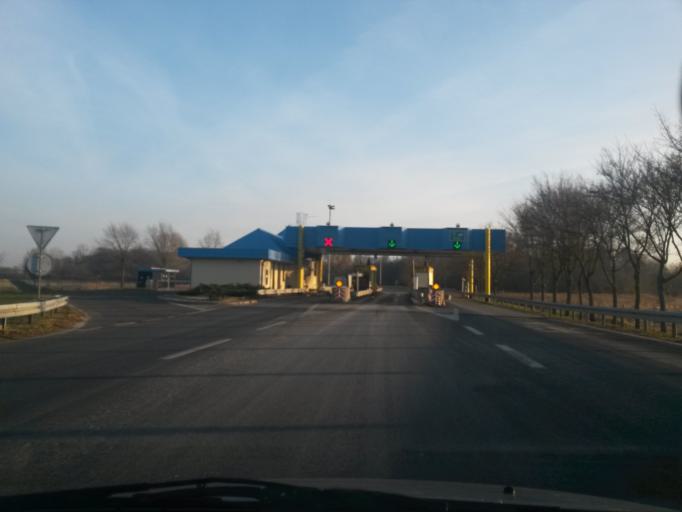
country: HR
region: Varazdinska
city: Jalzabet
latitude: 46.2839
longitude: 16.4847
